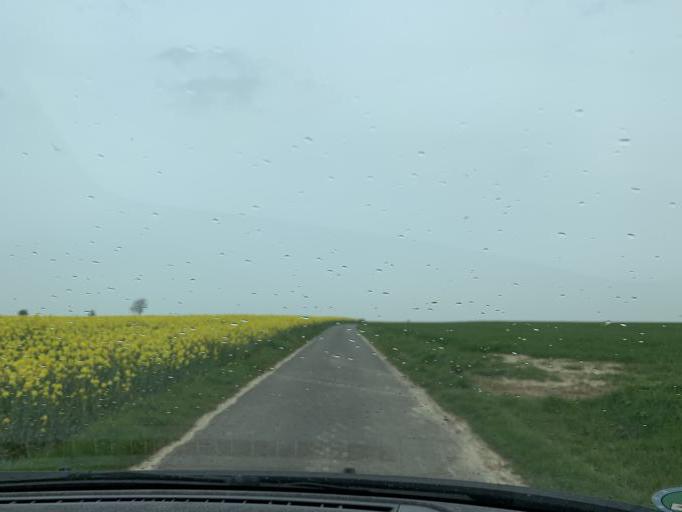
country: FR
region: Haute-Normandie
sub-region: Departement de la Seine-Maritime
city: Fontaine-le-Dun
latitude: 49.8562
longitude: 0.8223
